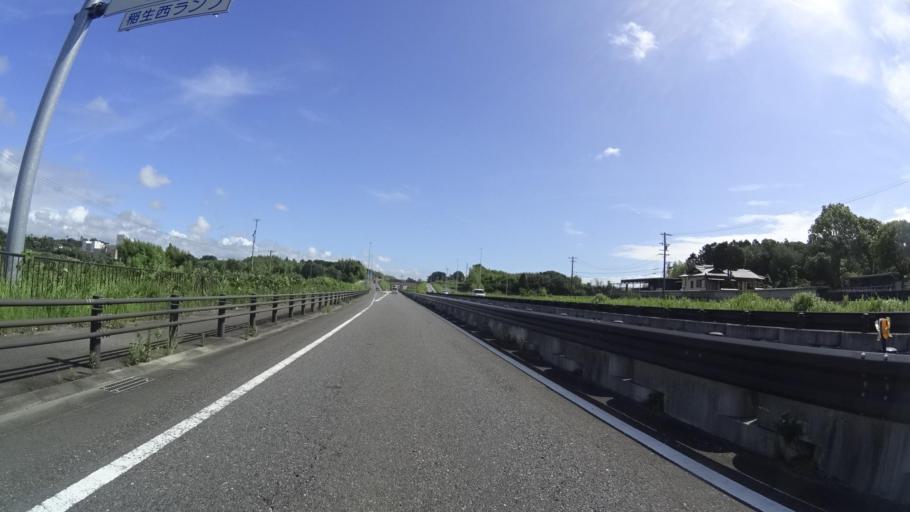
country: JP
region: Mie
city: Kawage
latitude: 34.8399
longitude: 136.5465
